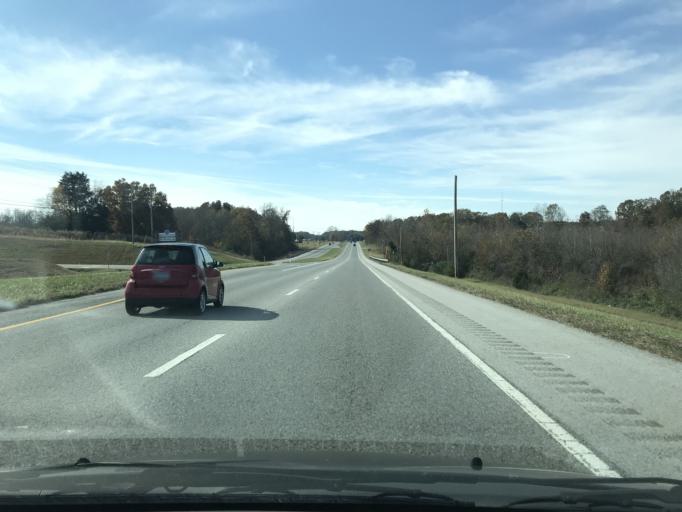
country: US
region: Tennessee
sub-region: Coffee County
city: Tullahoma
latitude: 35.4037
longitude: -86.1311
